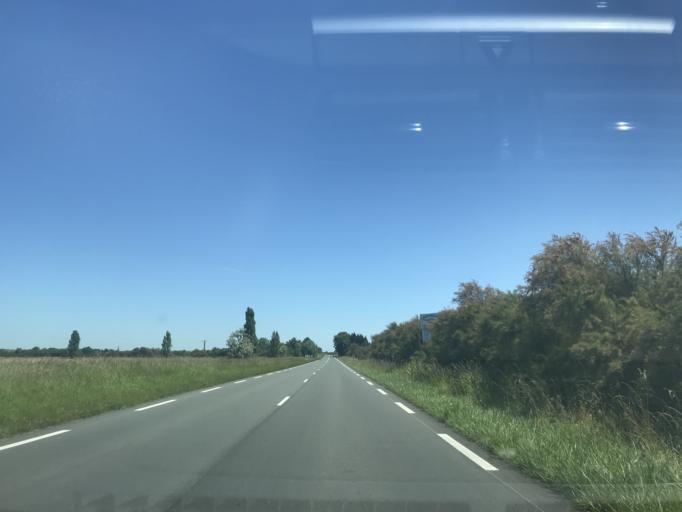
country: FR
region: Poitou-Charentes
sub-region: Departement de la Charente-Maritime
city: Meschers-sur-Gironde
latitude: 45.5558
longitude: -0.9233
